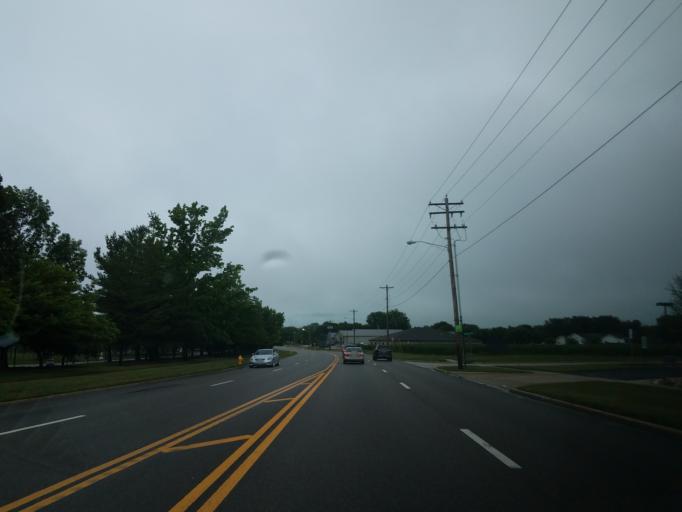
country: US
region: Illinois
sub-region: McLean County
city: Bloomington
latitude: 40.4503
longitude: -88.9904
